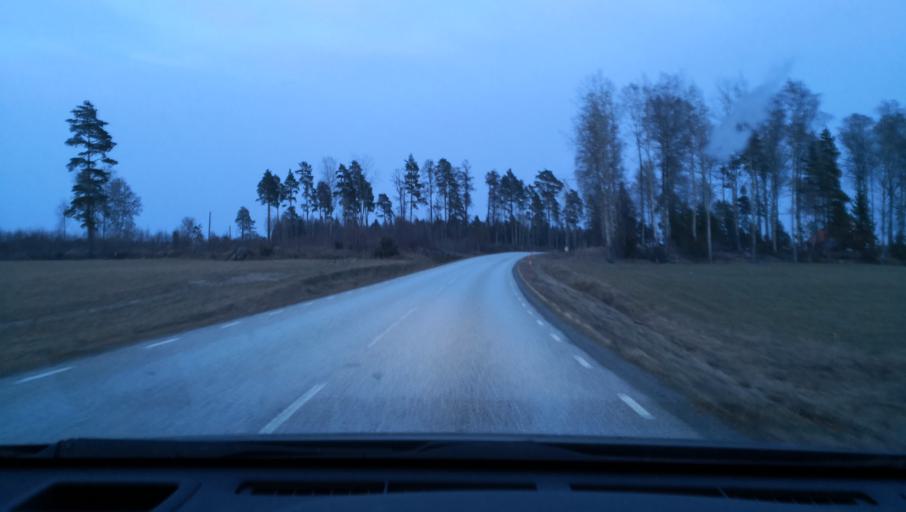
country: SE
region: OErebro
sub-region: Lindesbergs Kommun
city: Lindesberg
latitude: 59.5944
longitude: 15.2924
